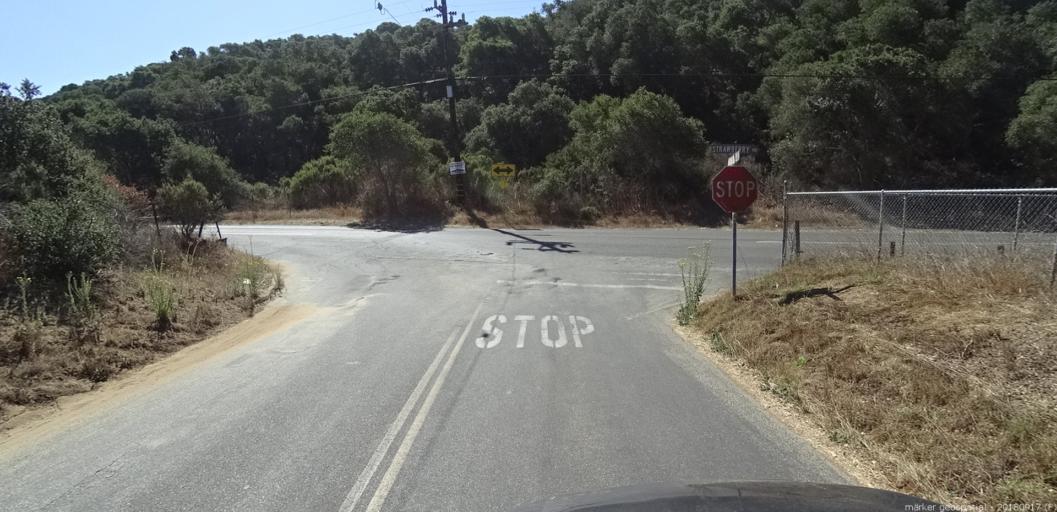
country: US
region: California
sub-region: Monterey County
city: Elkhorn
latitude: 36.8325
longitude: -121.6946
